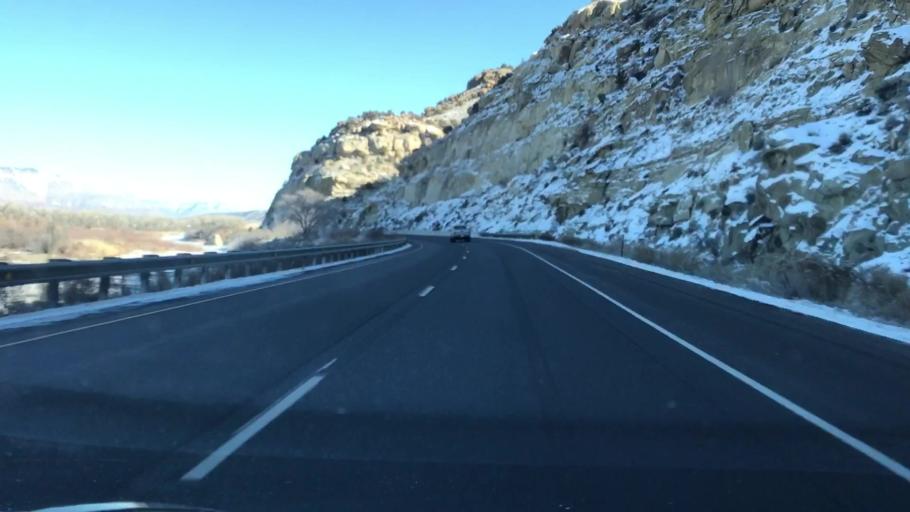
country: US
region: Colorado
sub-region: Mesa County
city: Palisade
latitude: 39.2741
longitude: -108.2443
